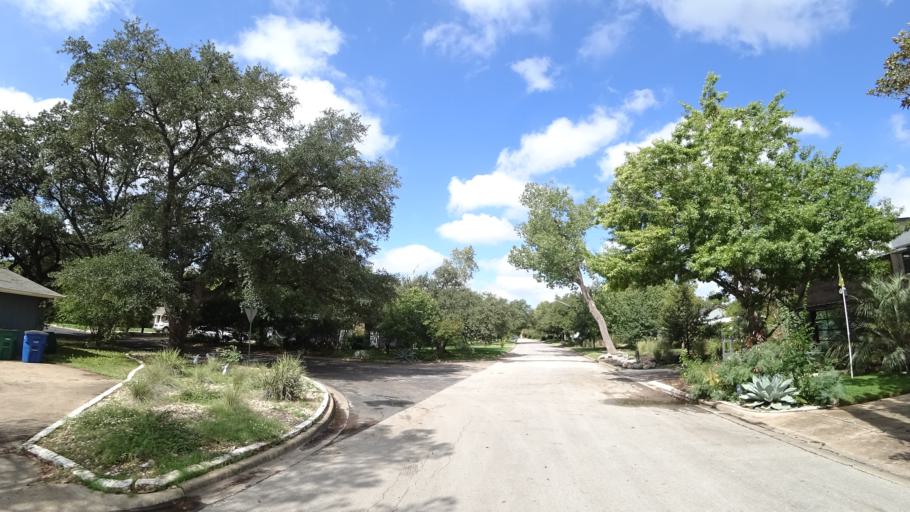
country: US
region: Texas
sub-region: Travis County
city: West Lake Hills
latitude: 30.3439
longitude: -97.7409
